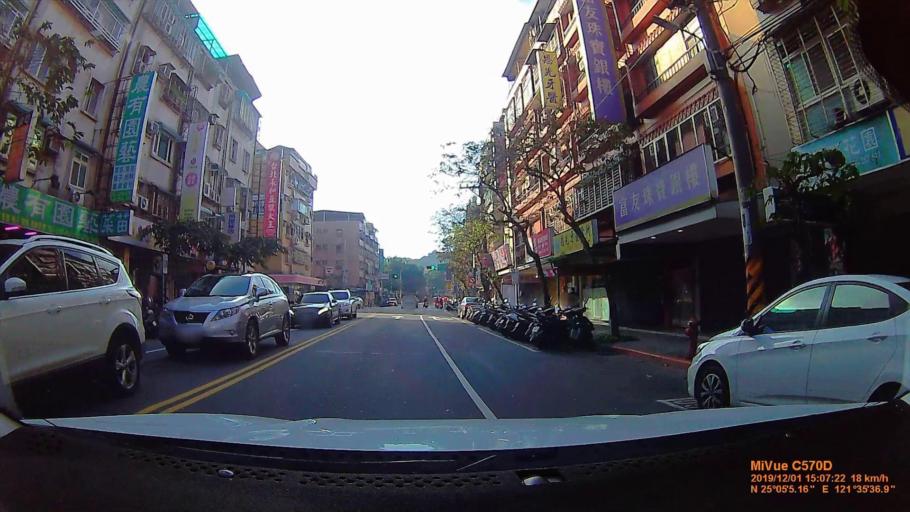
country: TW
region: Taipei
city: Taipei
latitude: 25.0848
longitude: 121.5936
